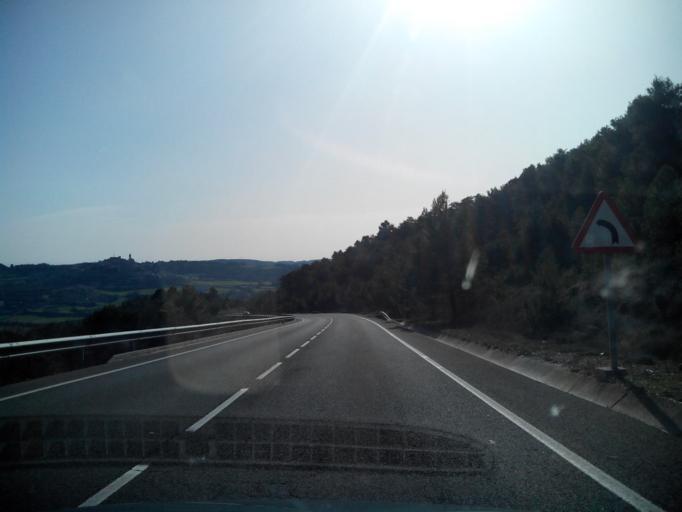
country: ES
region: Catalonia
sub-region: Provincia de Tarragona
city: Santa Coloma de Queralt
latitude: 41.5603
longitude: 1.4005
